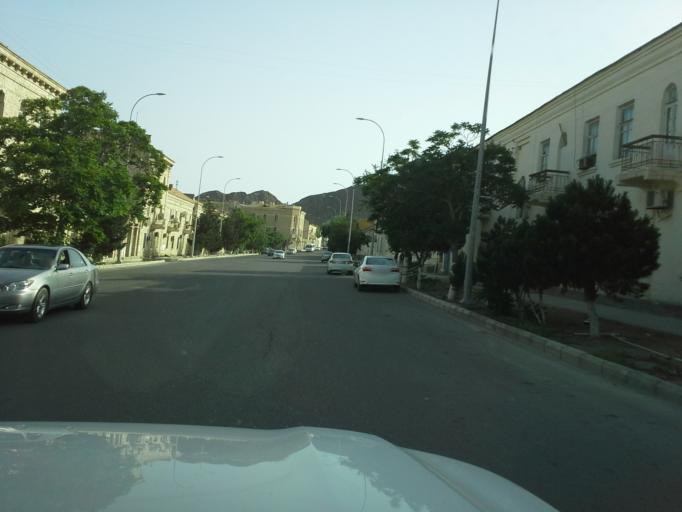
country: TM
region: Balkan
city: Turkmenbasy
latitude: 40.0042
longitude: 52.9912
